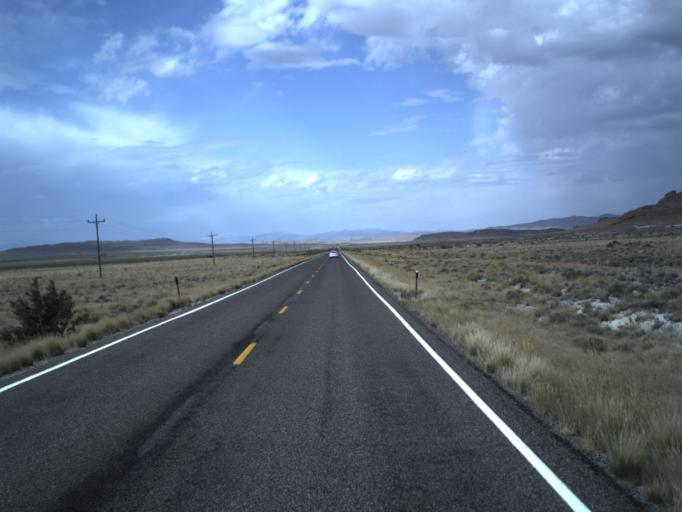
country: US
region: Utah
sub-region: Tooele County
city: Wendover
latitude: 41.4295
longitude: -113.8131
